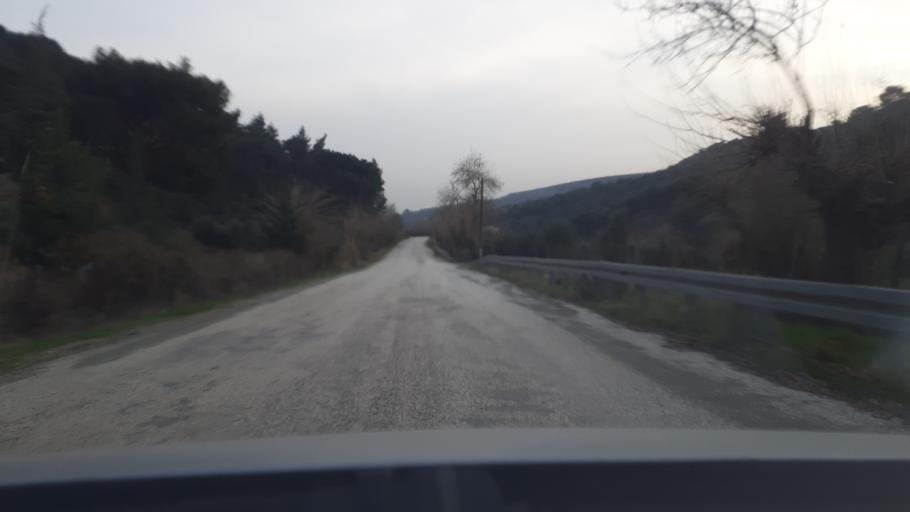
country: TR
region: Hatay
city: Kirikhan
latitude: 36.5210
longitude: 36.3182
